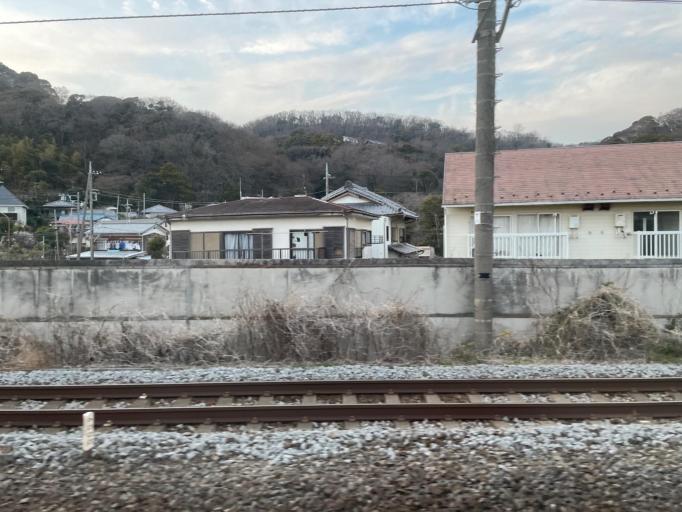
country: JP
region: Kanagawa
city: Oiso
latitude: 35.3132
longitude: 139.3160
